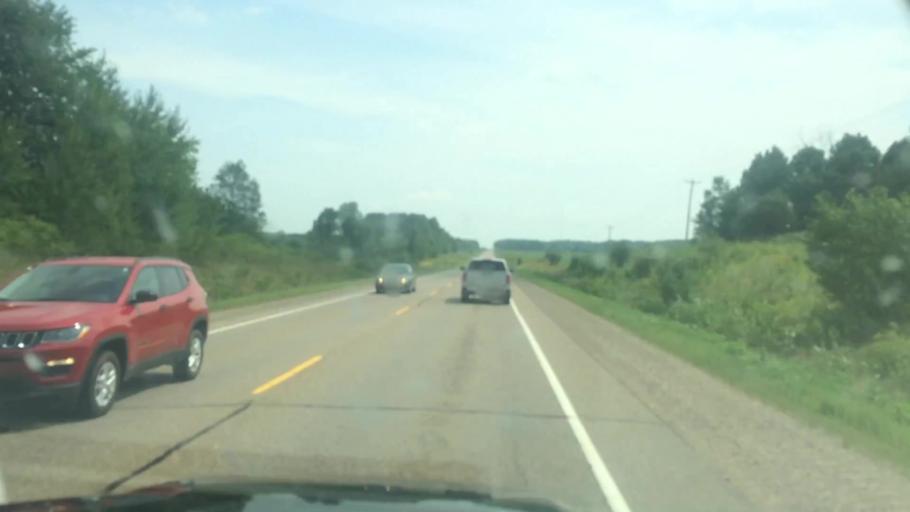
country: US
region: Wisconsin
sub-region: Langlade County
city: Antigo
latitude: 45.1680
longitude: -88.9215
